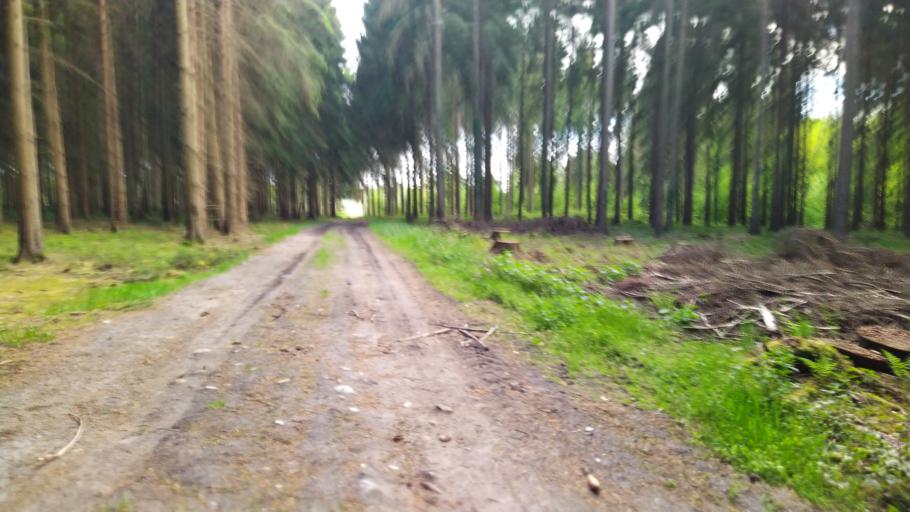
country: DE
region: Lower Saxony
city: Brest
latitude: 53.4127
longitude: 9.3737
